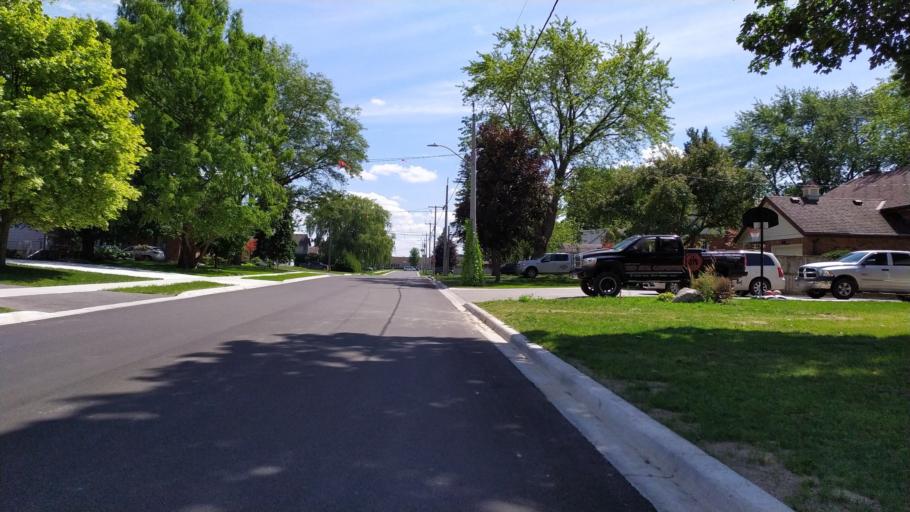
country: CA
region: Ontario
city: Stratford
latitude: 43.3736
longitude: -80.9564
